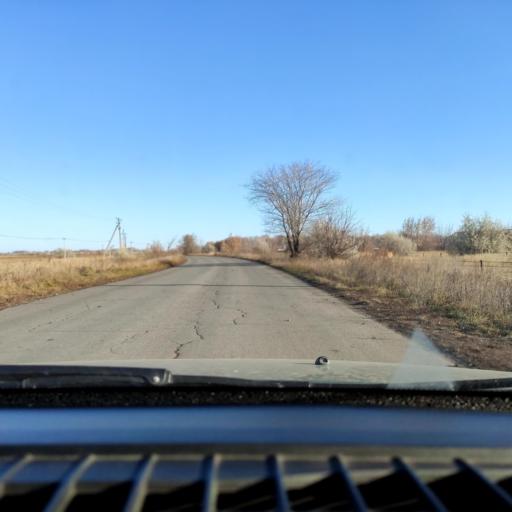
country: RU
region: Samara
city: Tol'yatti
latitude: 53.6452
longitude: 49.3179
